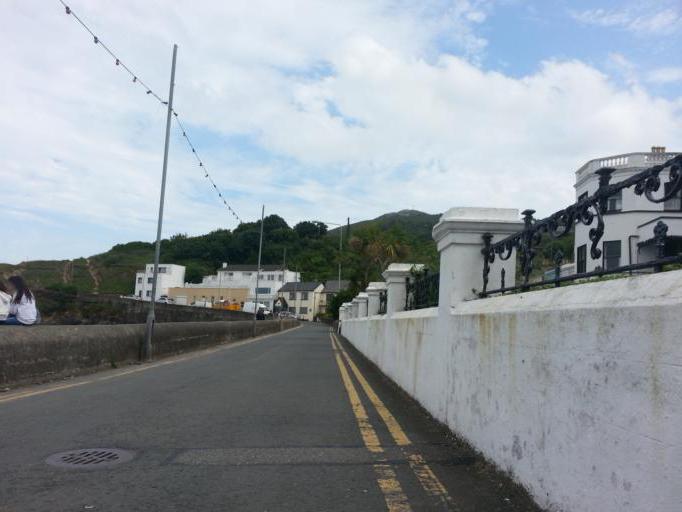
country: IE
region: Leinster
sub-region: Wicklow
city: Bray
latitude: 53.1967
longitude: -6.0929
